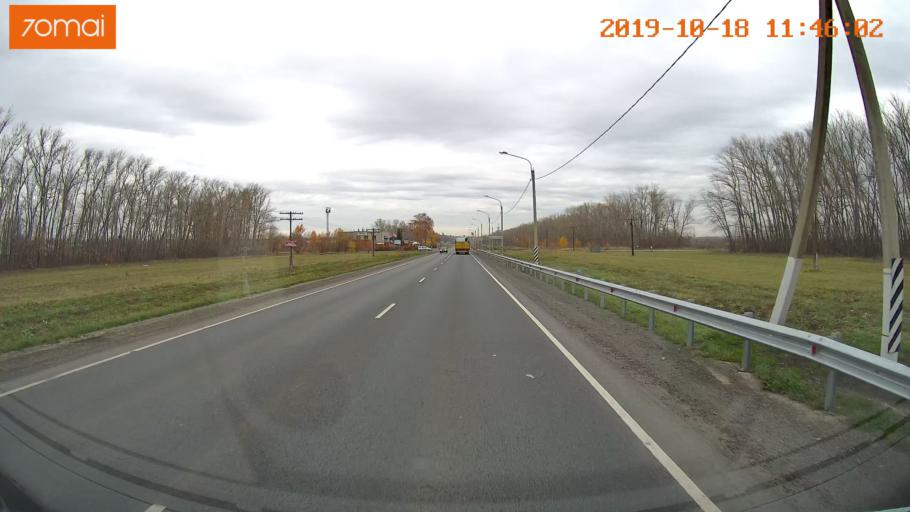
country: RU
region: Rjazan
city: Mikhaylov
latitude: 54.2160
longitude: 38.9782
